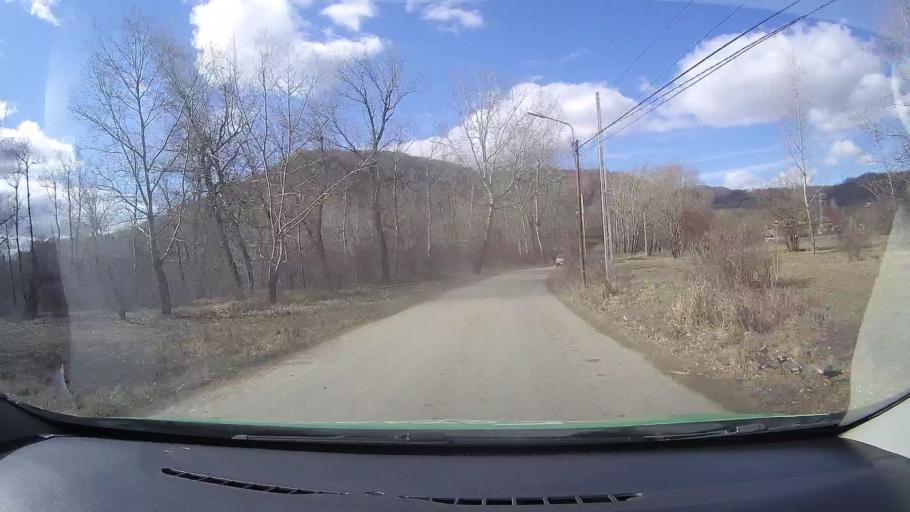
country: RO
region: Dambovita
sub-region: Oras Pucioasa
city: Pucioasa
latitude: 45.0668
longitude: 25.4264
